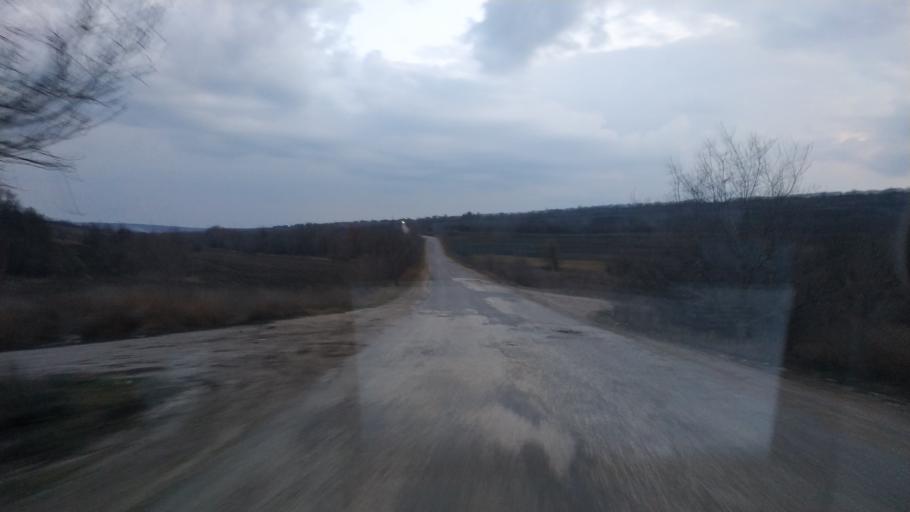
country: MD
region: Anenii Noi
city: Anenii Noi
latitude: 46.9496
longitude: 29.2824
